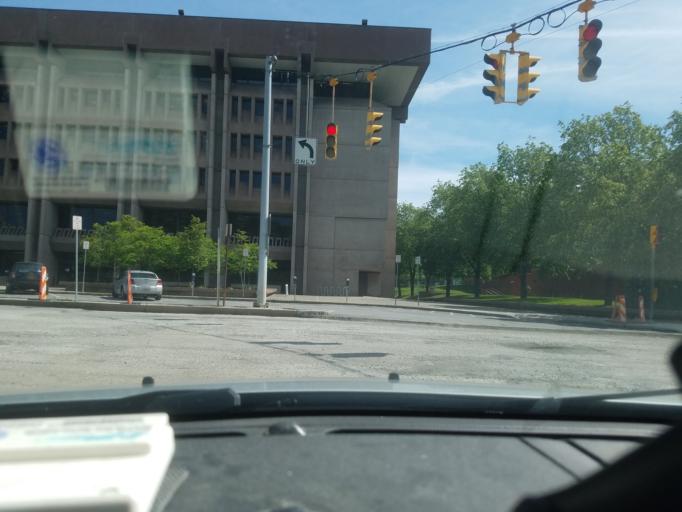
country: US
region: New York
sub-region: Onondaga County
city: Syracuse
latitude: 43.0407
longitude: -76.1329
